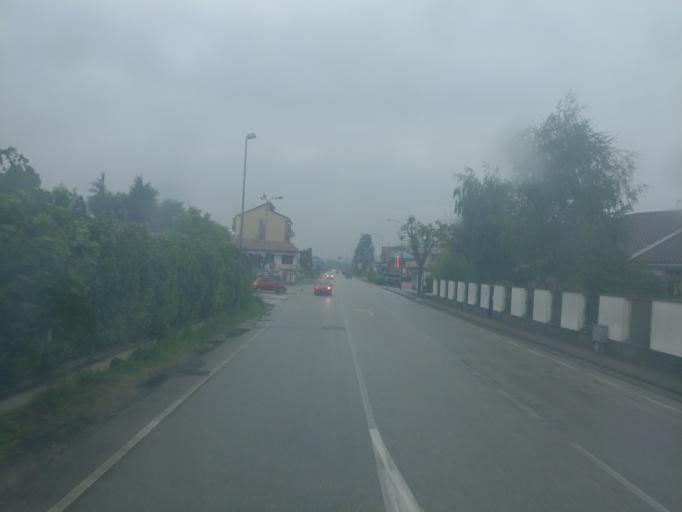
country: IT
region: Piedmont
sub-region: Provincia di Torino
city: La Loggia
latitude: 44.9602
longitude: 7.6677
